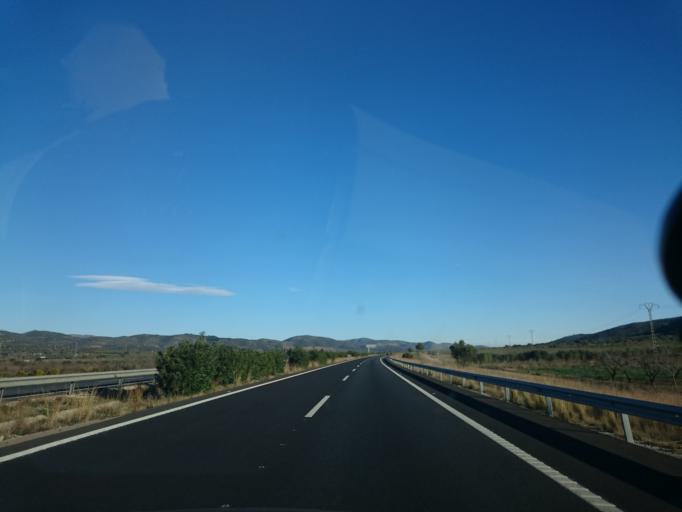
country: ES
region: Valencia
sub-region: Provincia de Castello
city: Alcala de Xivert
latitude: 40.3054
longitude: 0.2387
